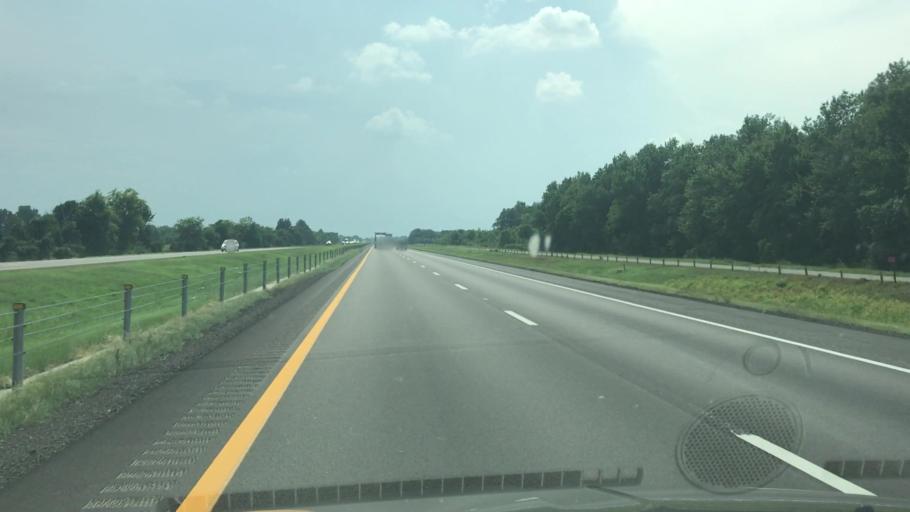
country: US
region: Arkansas
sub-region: Crittenden County
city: Earle
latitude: 35.1476
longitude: -90.4099
